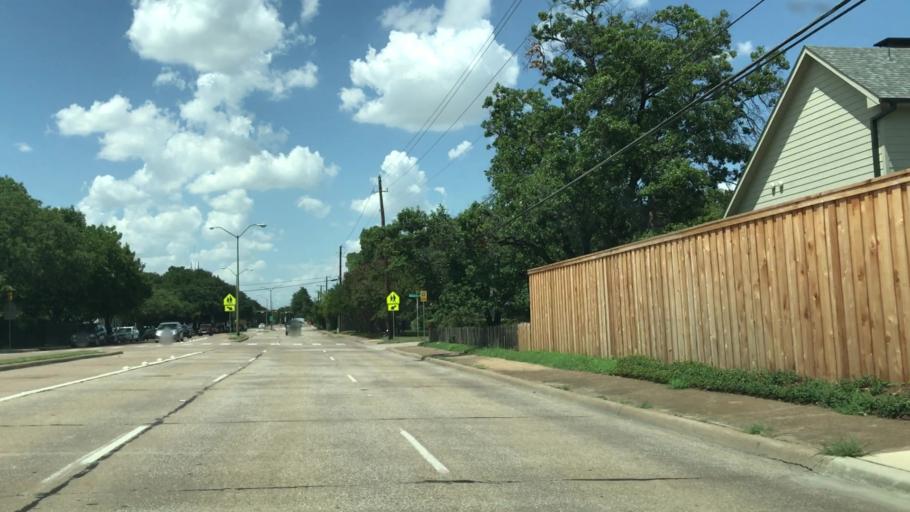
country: US
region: Texas
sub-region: Dallas County
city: University Park
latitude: 32.8774
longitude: -96.8384
